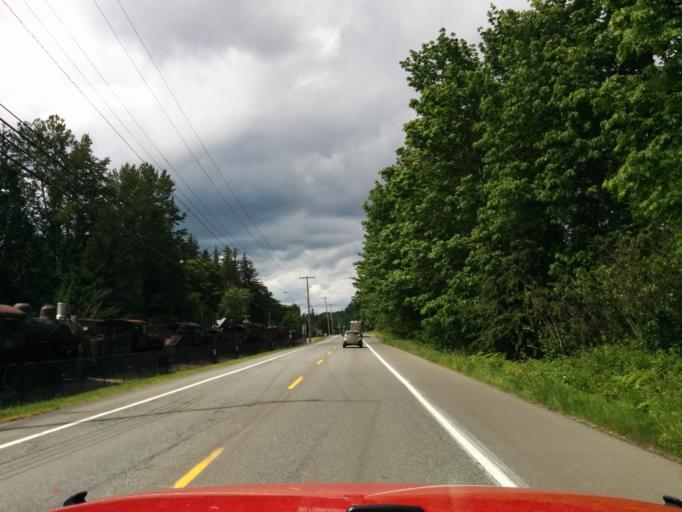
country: US
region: Washington
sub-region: King County
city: Snoqualmie
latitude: 47.5326
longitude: -121.8282
